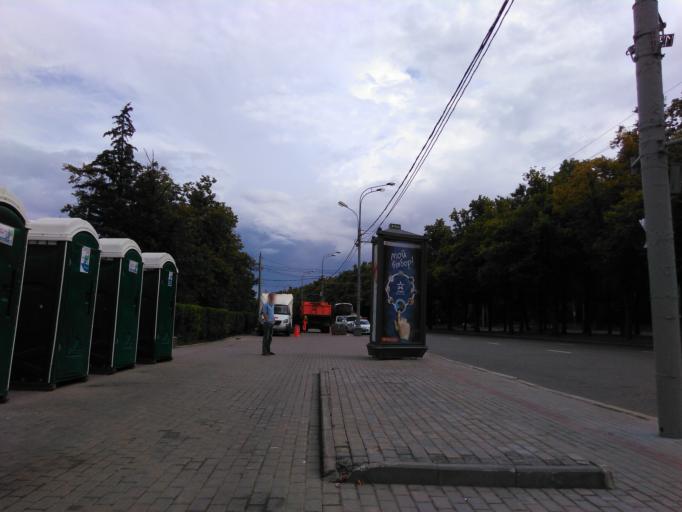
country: RU
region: Moscow
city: Luzhniki
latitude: 55.7082
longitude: 37.5444
